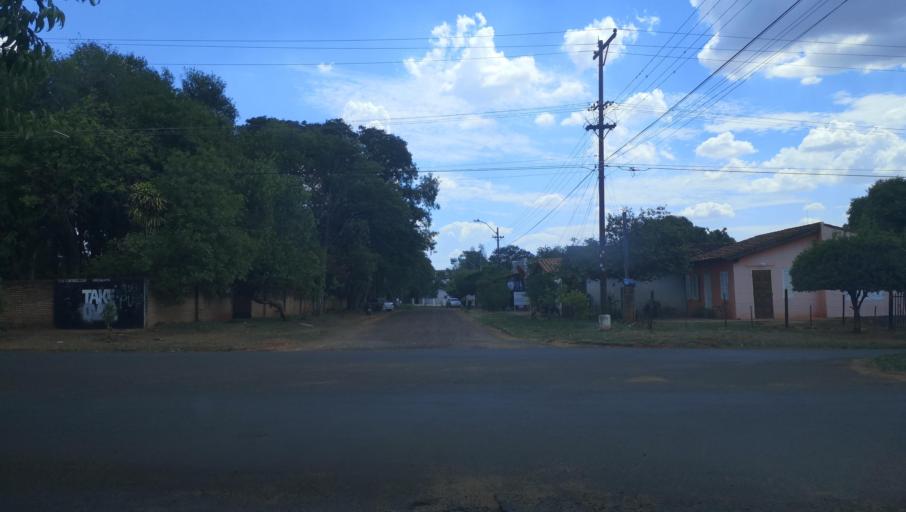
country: PY
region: Misiones
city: Santa Maria
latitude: -26.8903
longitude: -57.0307
